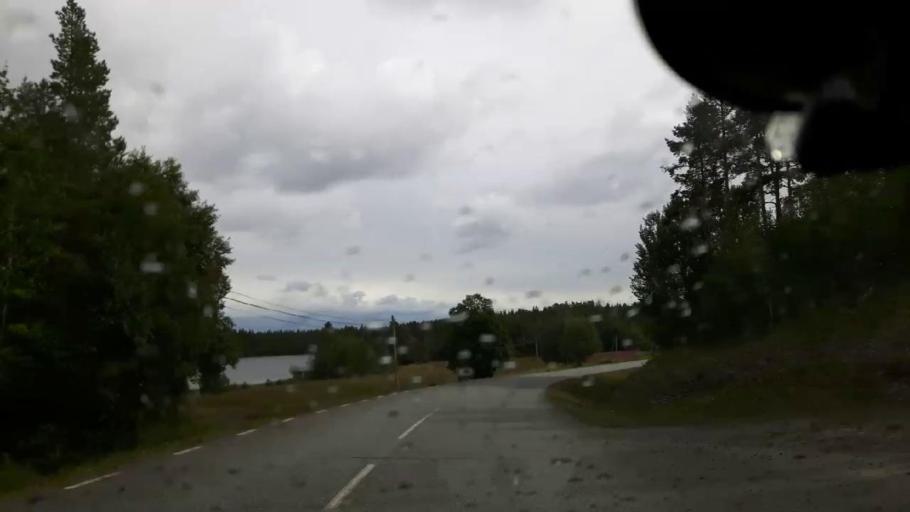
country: SE
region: Jaemtland
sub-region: Krokoms Kommun
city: Valla
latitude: 63.3967
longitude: 13.8177
